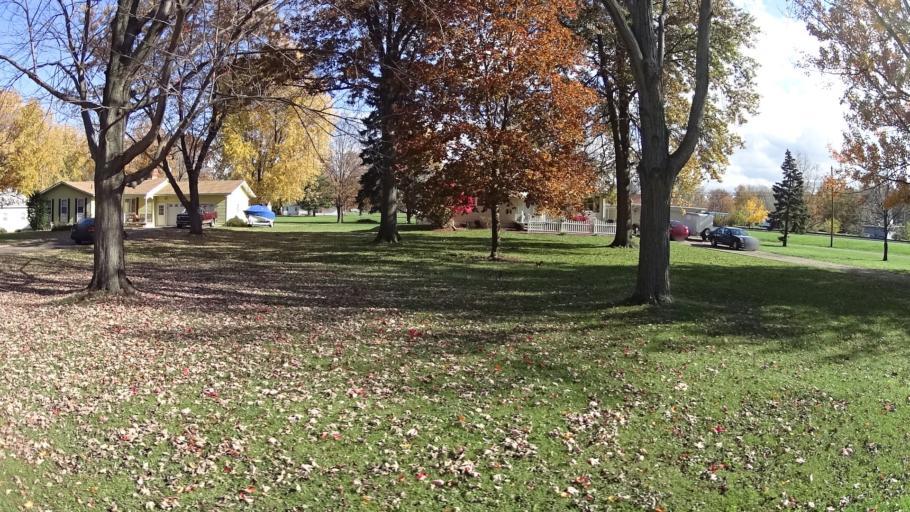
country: US
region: Ohio
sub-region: Lorain County
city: Lorain
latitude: 41.4519
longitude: -82.2084
